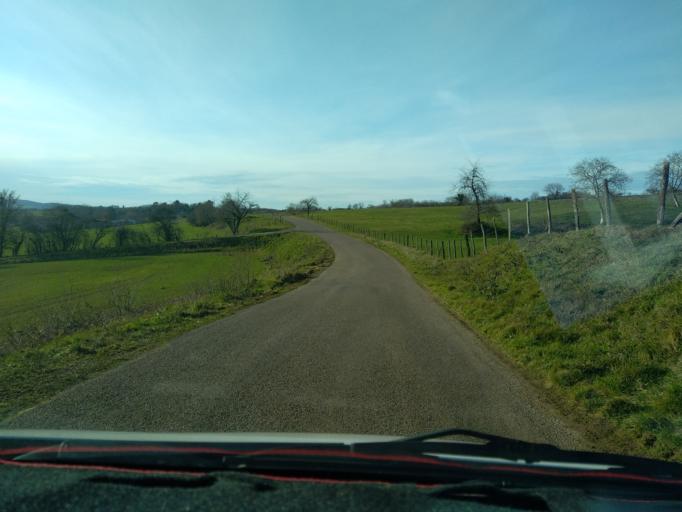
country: FR
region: Franche-Comte
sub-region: Departement de la Haute-Saone
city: Marnay
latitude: 47.3069
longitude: 5.6721
